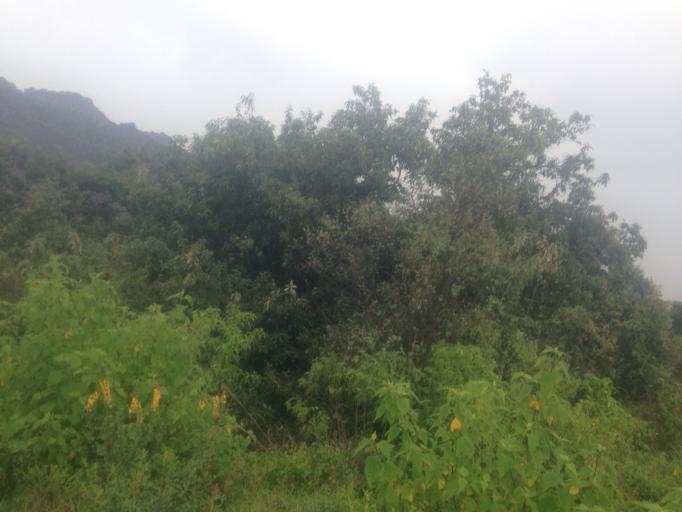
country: MX
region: Nayarit
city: Jala
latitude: 21.1366
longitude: -104.5001
